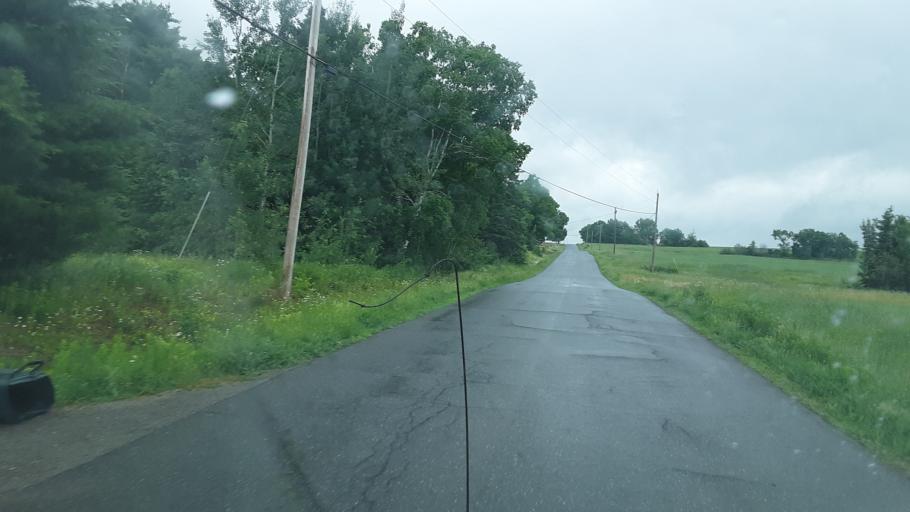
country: US
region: Maine
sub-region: Aroostook County
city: Presque Isle
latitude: 46.6816
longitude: -68.1943
